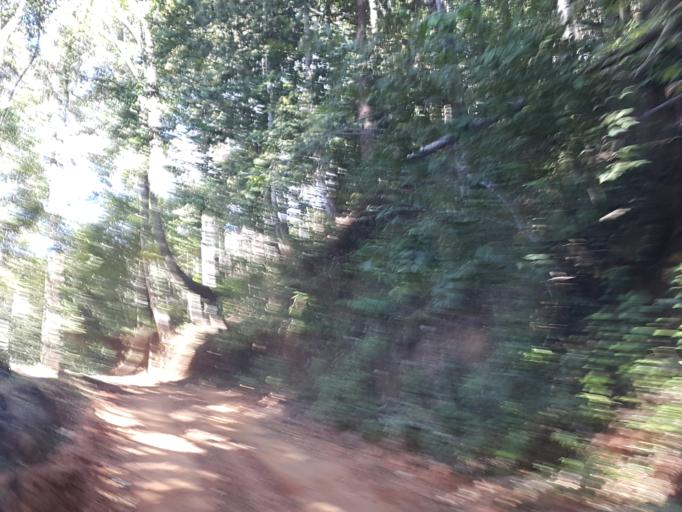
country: TH
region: Chiang Mai
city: Wiang Haeng
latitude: 19.5298
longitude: 98.8108
